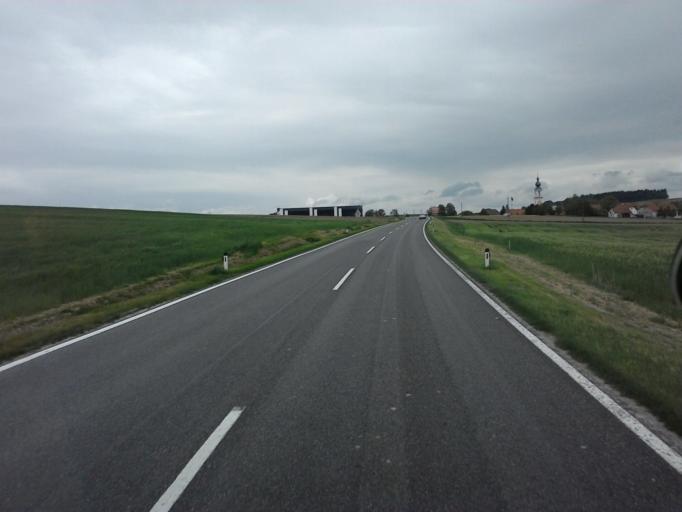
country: AT
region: Upper Austria
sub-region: Politischer Bezirk Vocklabruck
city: Wolfsegg am Hausruck
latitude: 48.2047
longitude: 13.6728
